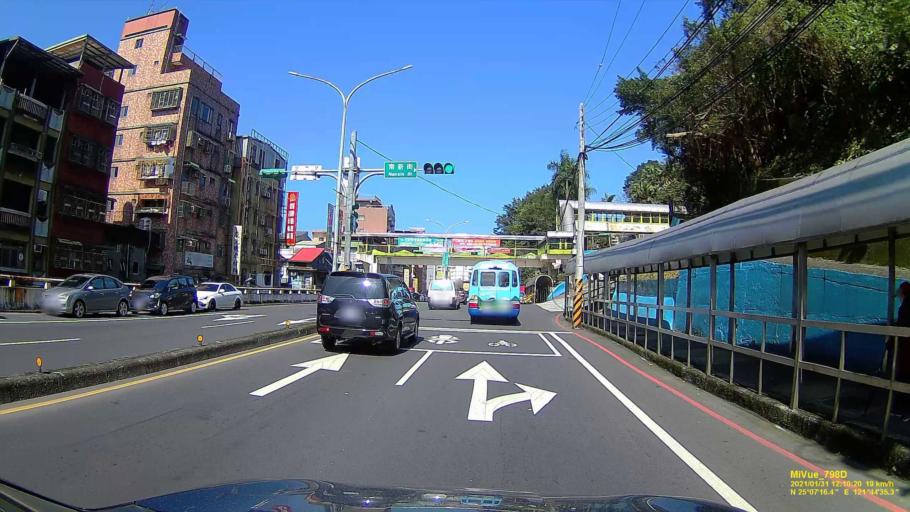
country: TW
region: Taiwan
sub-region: Keelung
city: Keelung
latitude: 25.1215
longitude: 121.7431
